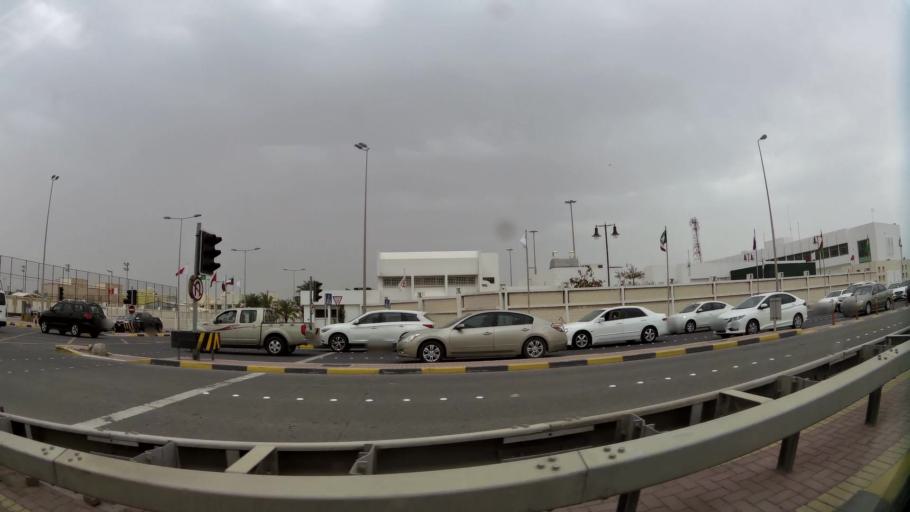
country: BH
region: Northern
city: Madinat `Isa
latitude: 26.1550
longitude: 50.5416
